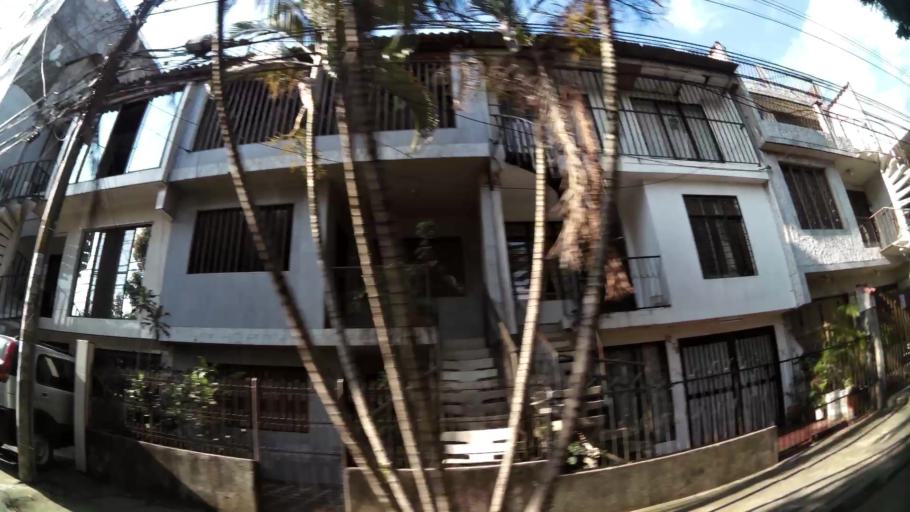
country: CO
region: Valle del Cauca
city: Cali
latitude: 3.4176
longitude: -76.5330
